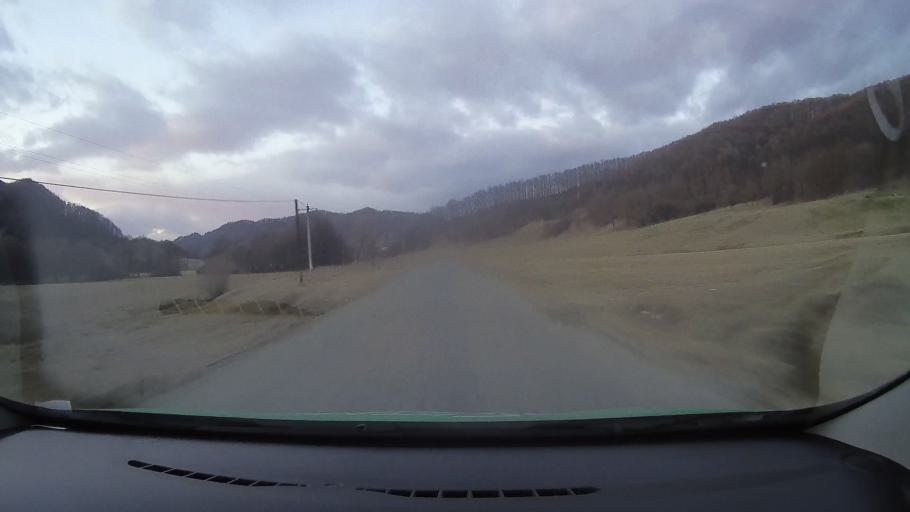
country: RO
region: Dambovita
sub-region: Comuna Valea Lunga
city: Valea Lunga-Cricov
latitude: 45.0904
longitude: 25.5798
